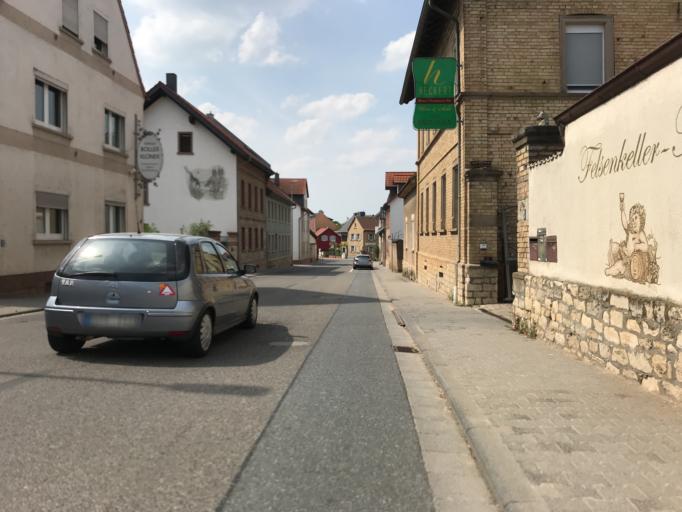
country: DE
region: Rheinland-Pfalz
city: Stadecken-Elsheim
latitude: 49.9088
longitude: 8.1375
